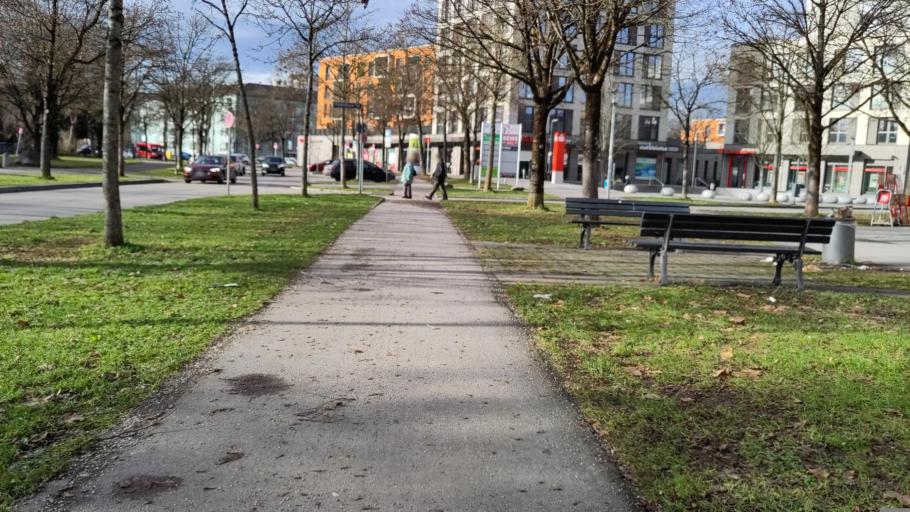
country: DE
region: Bavaria
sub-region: Upper Bavaria
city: Neuried
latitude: 48.0951
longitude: 11.4971
